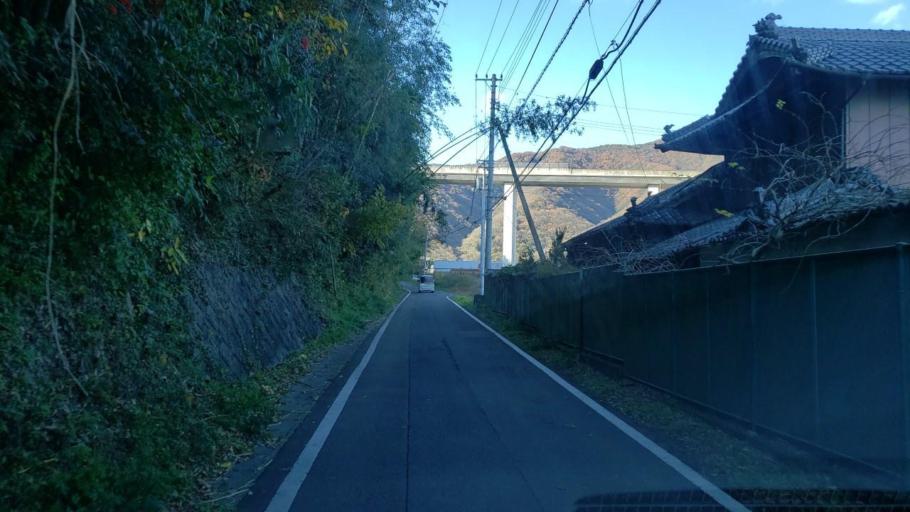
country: JP
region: Tokushima
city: Wakimachi
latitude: 34.0679
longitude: 134.0866
